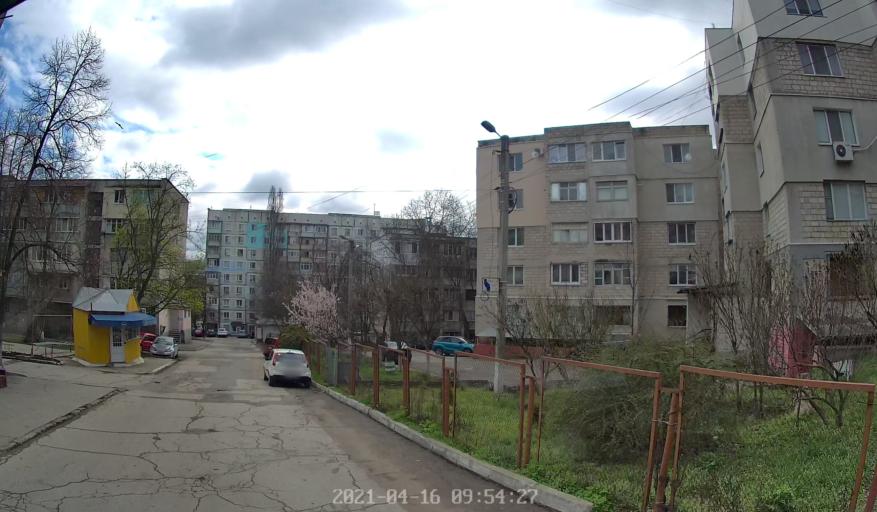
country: MD
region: Chisinau
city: Stauceni
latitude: 47.0574
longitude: 28.8451
